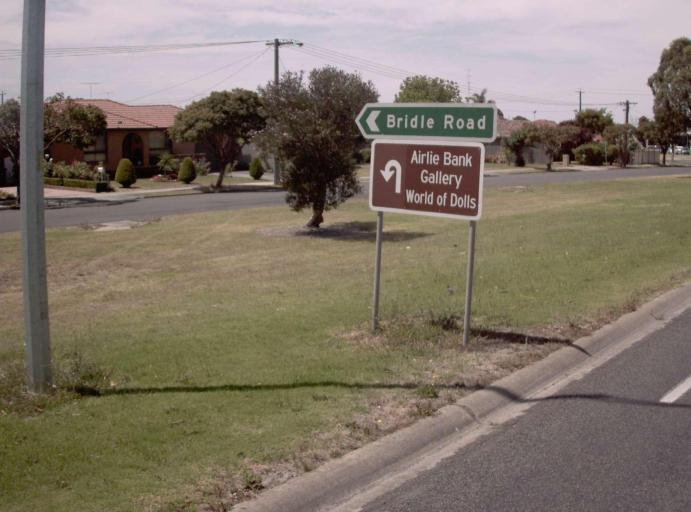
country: AU
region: Victoria
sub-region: Latrobe
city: Morwell
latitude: -38.2350
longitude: 146.4300
